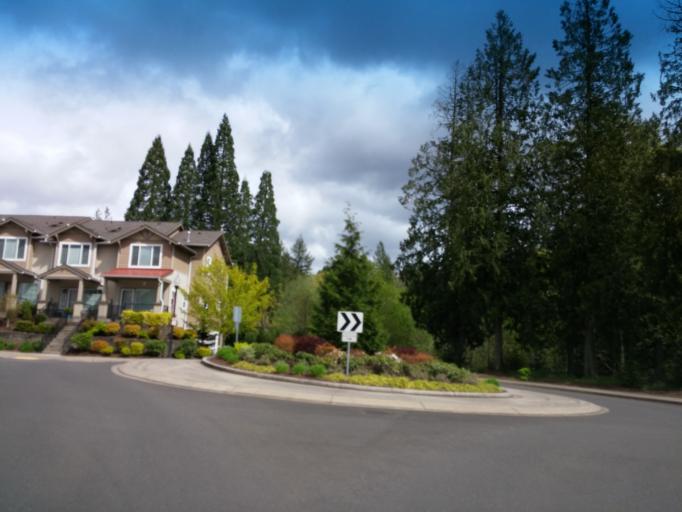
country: US
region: Oregon
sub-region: Washington County
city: Cedar Mill
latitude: 45.5211
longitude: -122.7967
